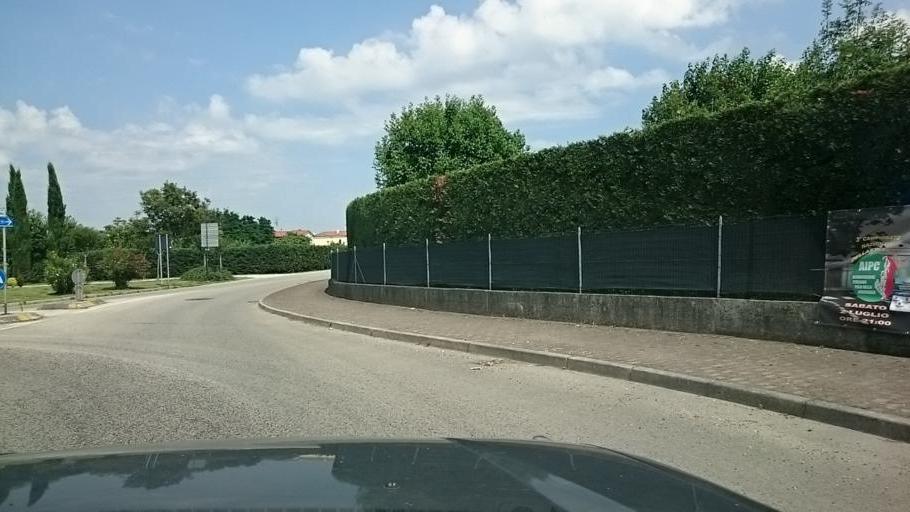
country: IT
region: Veneto
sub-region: Provincia di Vicenza
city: Cartigliano
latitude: 45.7220
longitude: 11.6976
